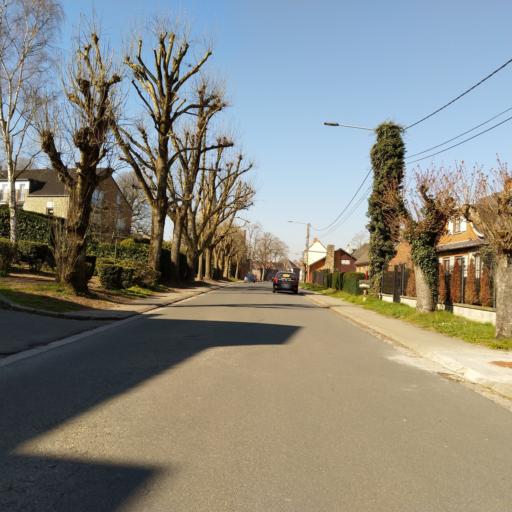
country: BE
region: Wallonia
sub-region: Province du Hainaut
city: Mons
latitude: 50.4774
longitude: 3.9600
